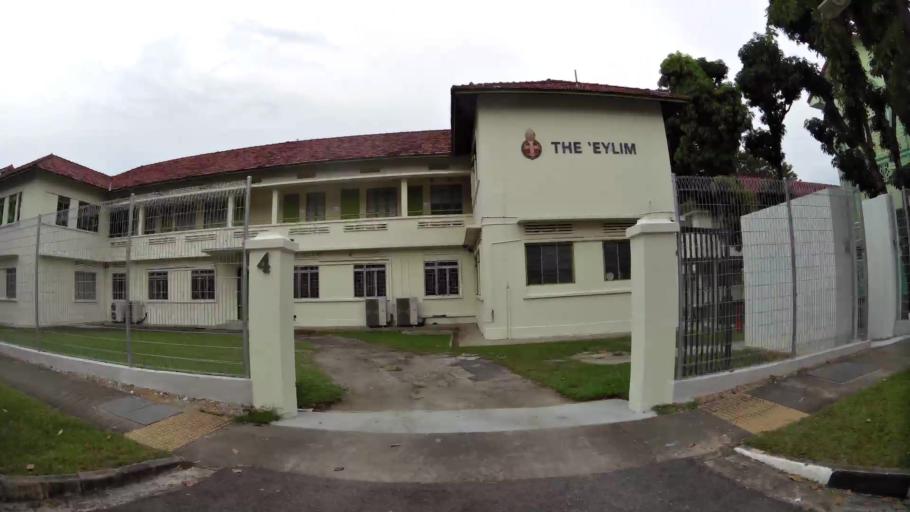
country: SG
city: Singapore
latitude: 1.3560
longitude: 103.8794
